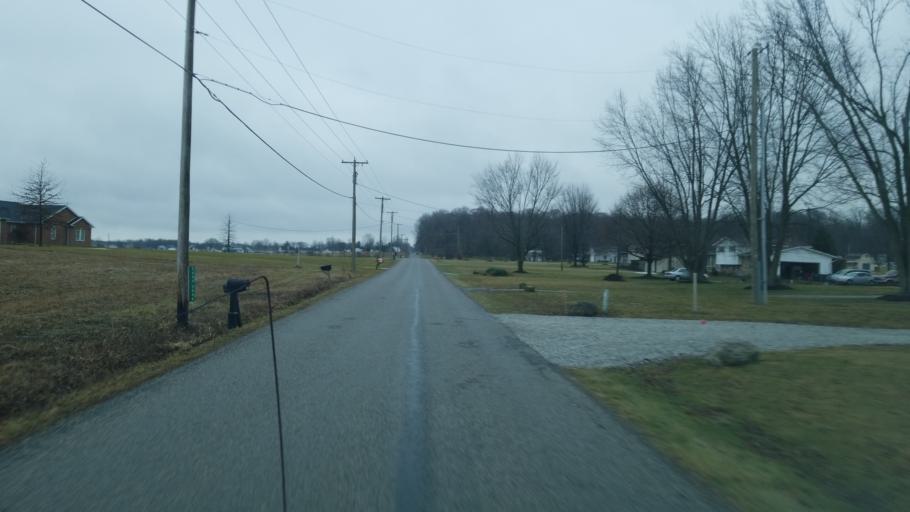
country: US
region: Ohio
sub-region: Wayne County
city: Orrville
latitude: 40.8698
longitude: -81.7840
